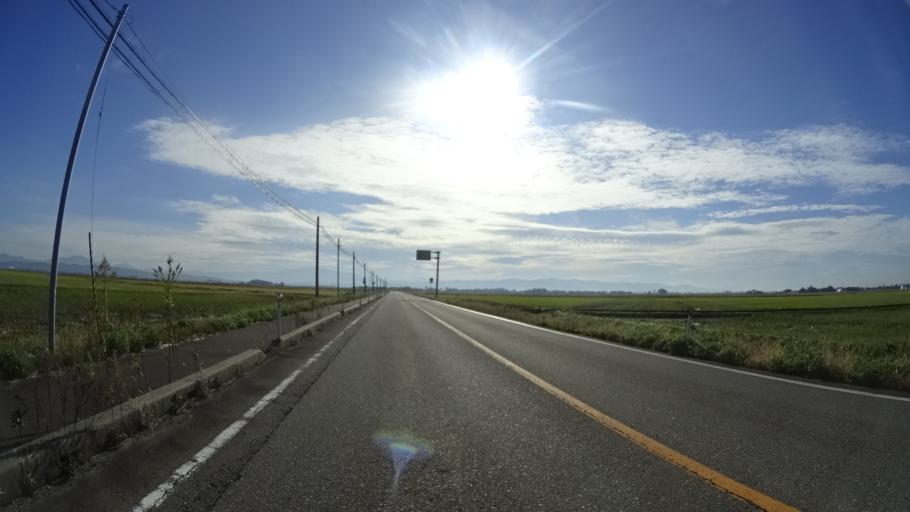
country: JP
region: Niigata
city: Mitsuke
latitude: 37.5692
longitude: 138.8424
